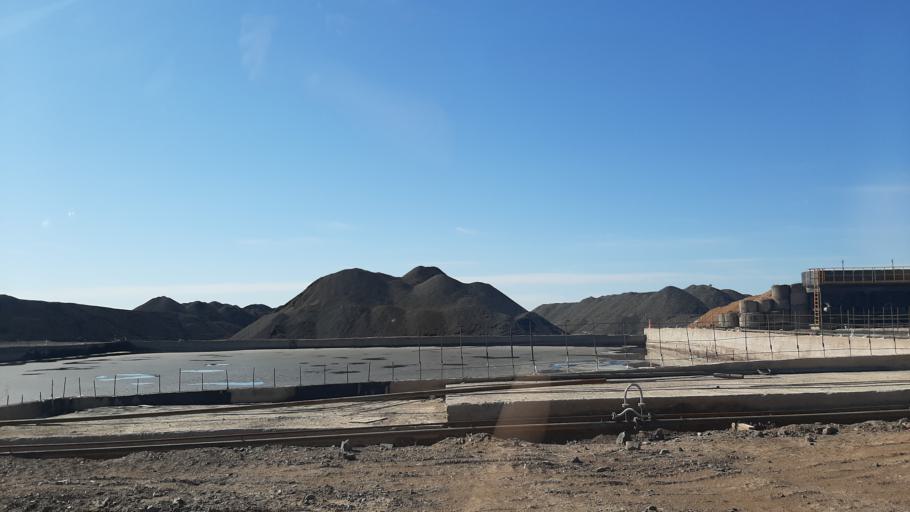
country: KZ
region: Almaty Oblysy
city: Ulken
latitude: 45.1607
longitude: 73.9411
